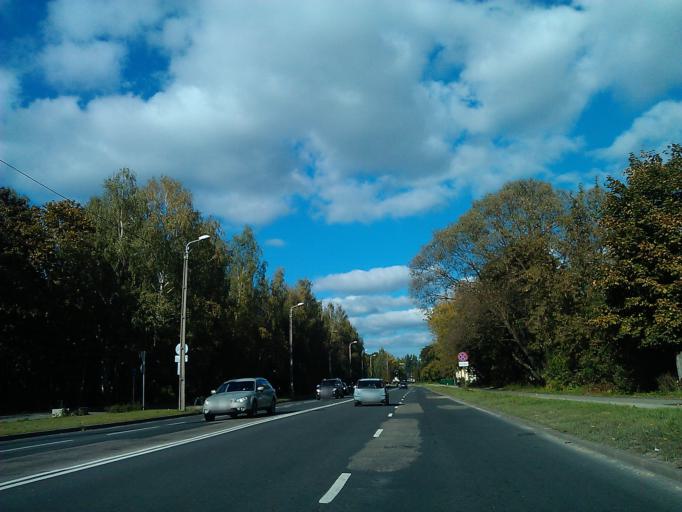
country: LV
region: Riga
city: Bergi
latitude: 56.9782
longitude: 24.2541
